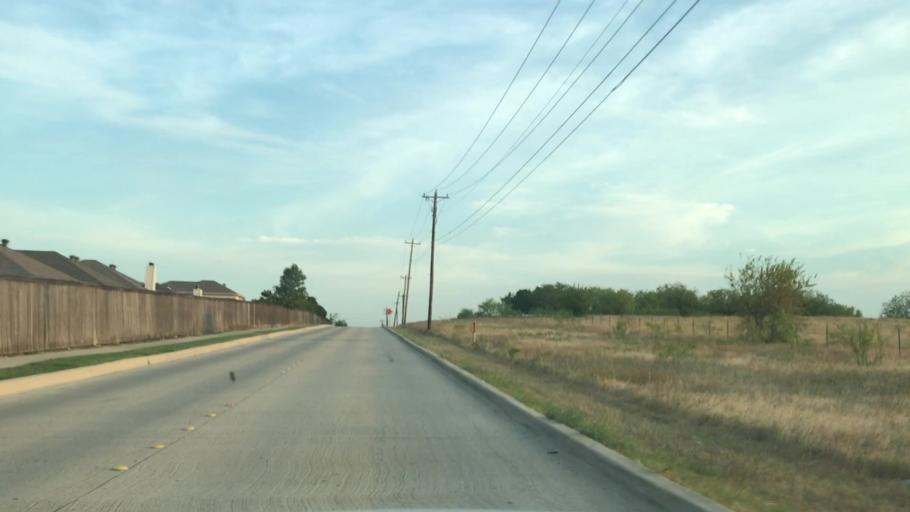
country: US
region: Texas
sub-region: Tarrant County
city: Keller
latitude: 32.9671
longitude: -97.2812
